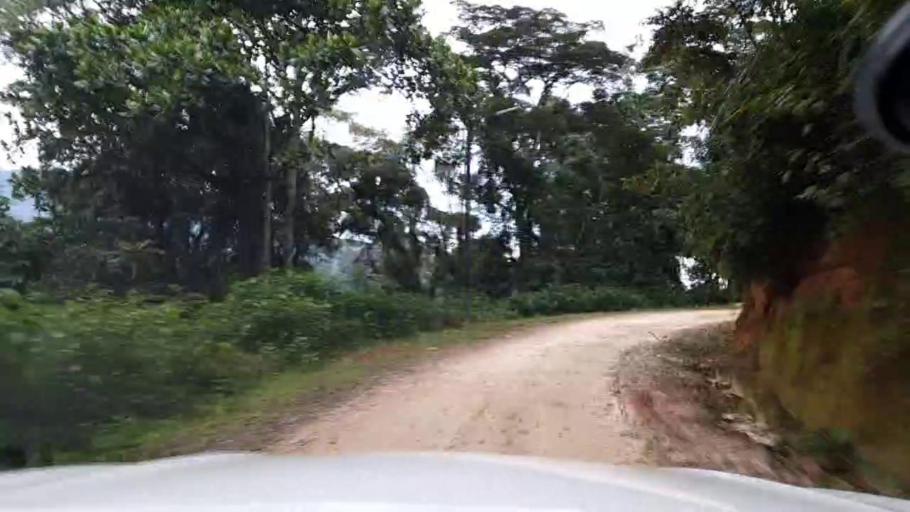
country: RW
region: Western Province
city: Cyangugu
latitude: -2.5645
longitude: 29.2286
